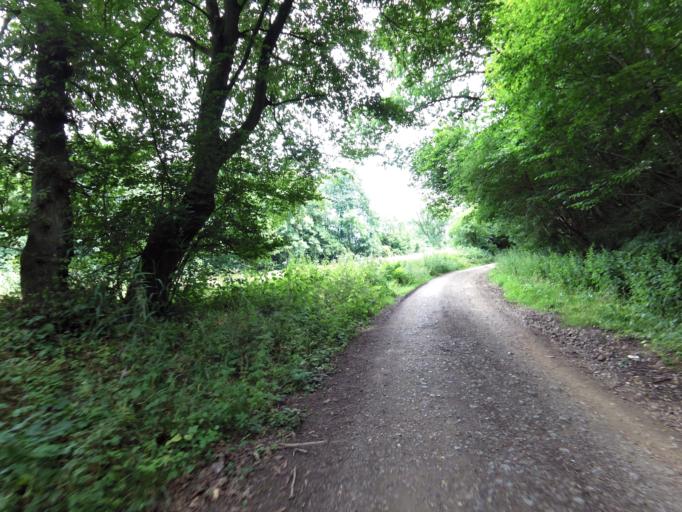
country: NL
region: Limburg
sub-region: Gemeente Simpelveld
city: Simpelveld
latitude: 50.8084
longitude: 5.9758
